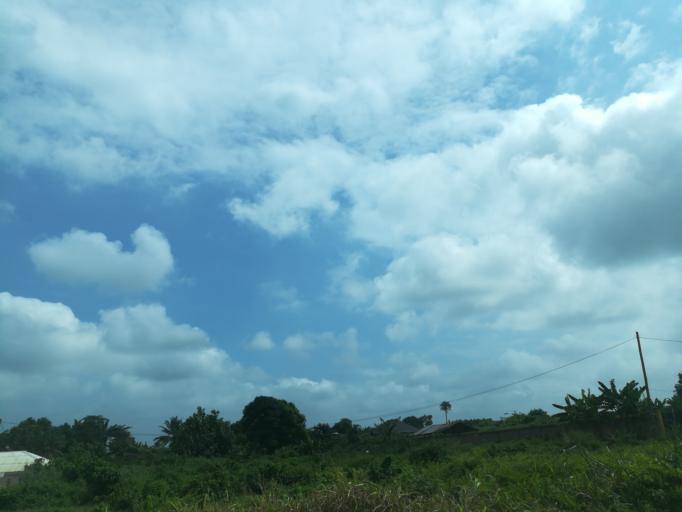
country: NG
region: Lagos
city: Ejirin
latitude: 6.6509
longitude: 3.7063
